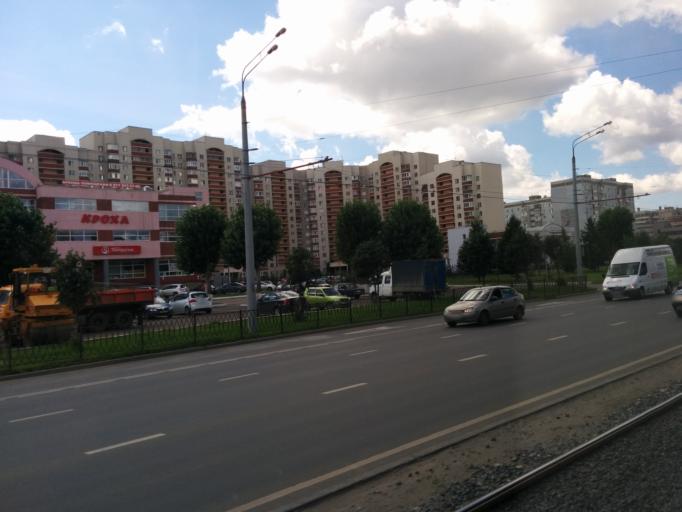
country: RU
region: Tatarstan
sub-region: Gorod Kazan'
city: Kazan
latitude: 55.8270
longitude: 49.1259
